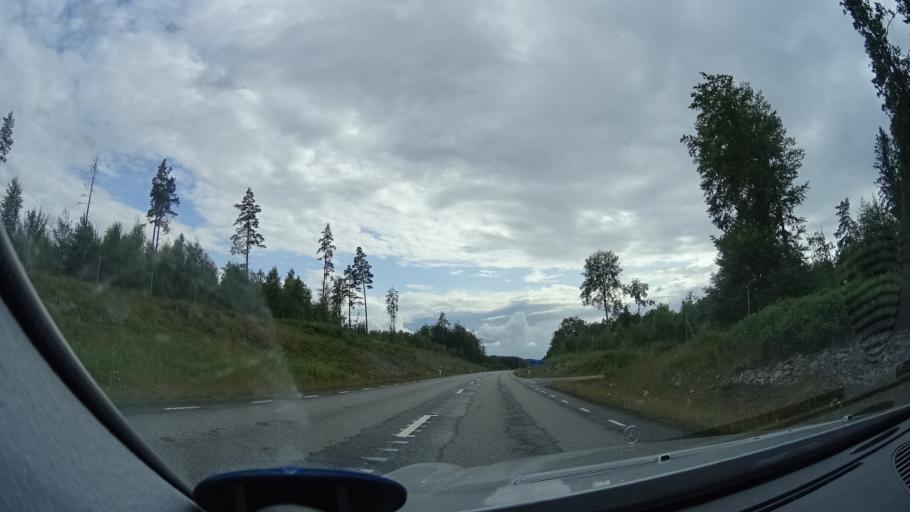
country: SE
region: Blekinge
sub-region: Karlshamns Kommun
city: Svangsta
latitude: 56.2749
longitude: 14.8610
